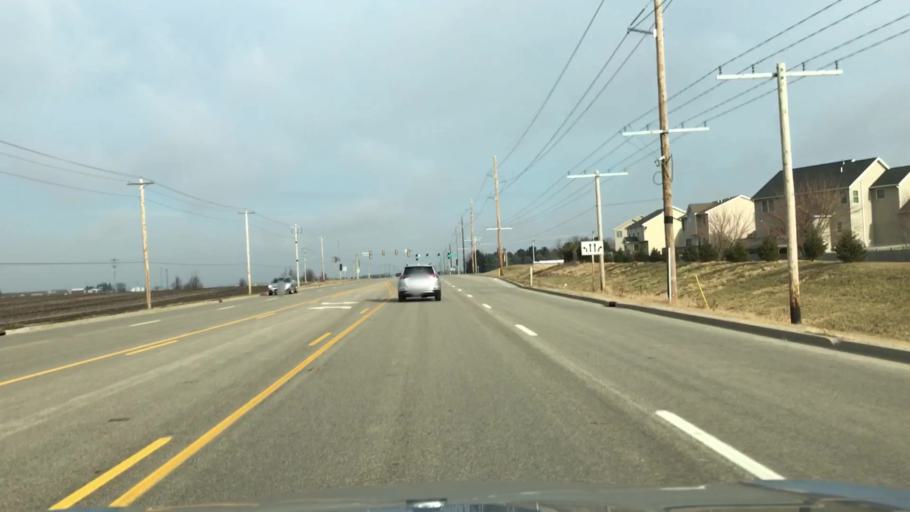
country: US
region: Illinois
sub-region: McLean County
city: Normal
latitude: 40.5151
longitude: -88.9028
